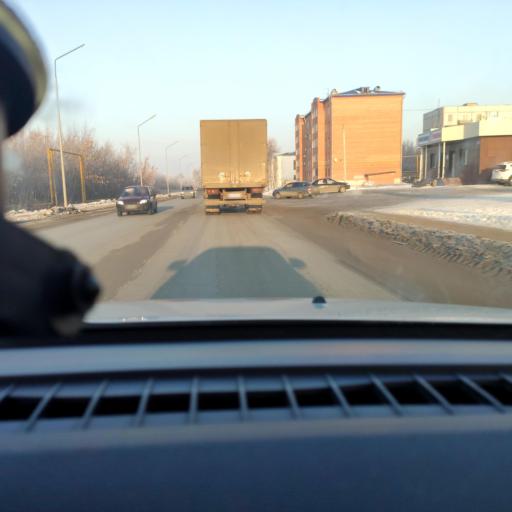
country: RU
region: Samara
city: Chapayevsk
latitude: 52.9701
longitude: 49.6979
